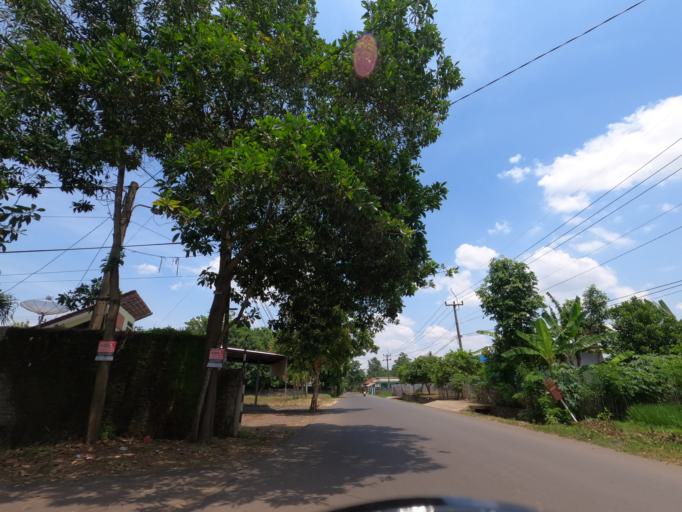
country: ID
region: West Java
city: Pamanukan
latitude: -6.5419
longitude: 107.7680
